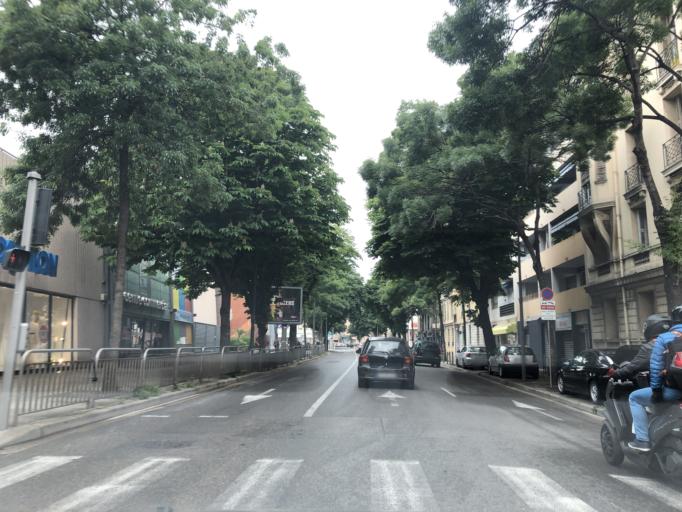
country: FR
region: Provence-Alpes-Cote d'Azur
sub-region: Departement des Alpes-Maritimes
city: Villefranche-sur-Mer
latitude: 43.7067
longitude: 7.2876
